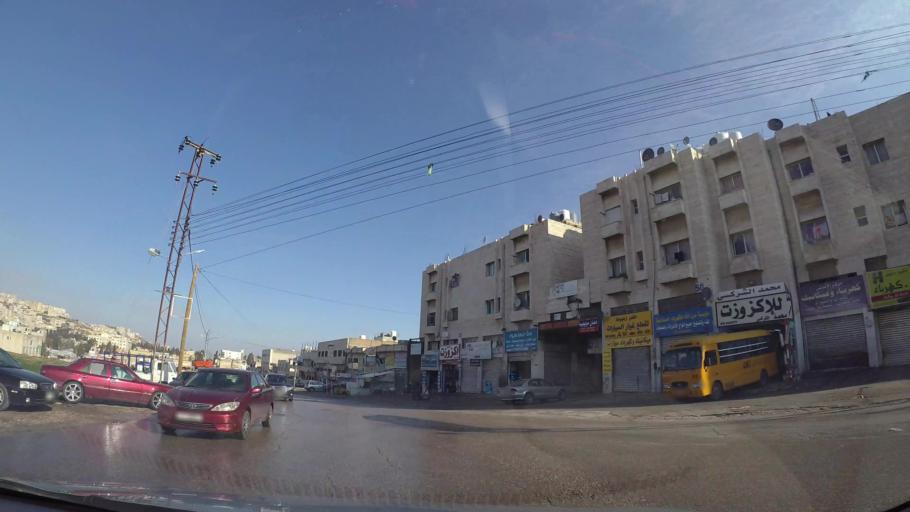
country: JO
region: Amman
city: Al Jubayhah
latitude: 32.0133
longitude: 35.8496
